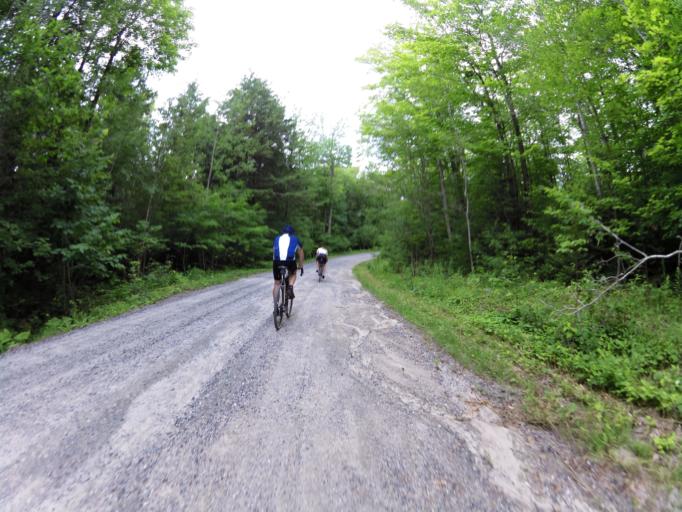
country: CA
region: Ontario
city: Perth
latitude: 45.0276
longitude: -76.5250
